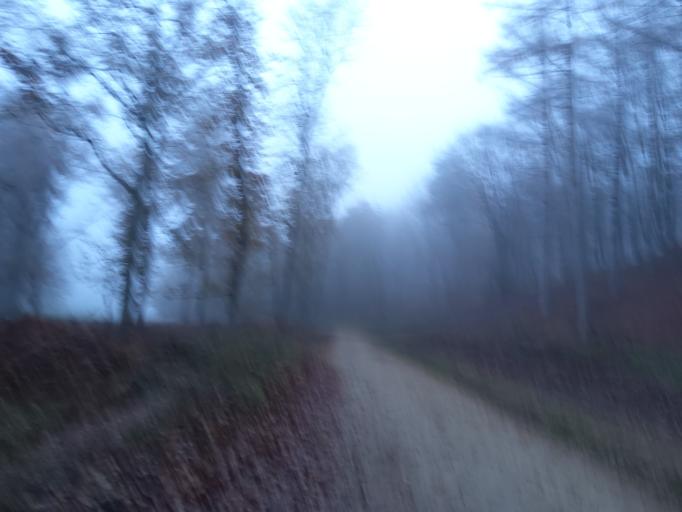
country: NL
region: Gelderland
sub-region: Gemeente Rheden
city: Rheden
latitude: 52.0198
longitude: 6.0232
